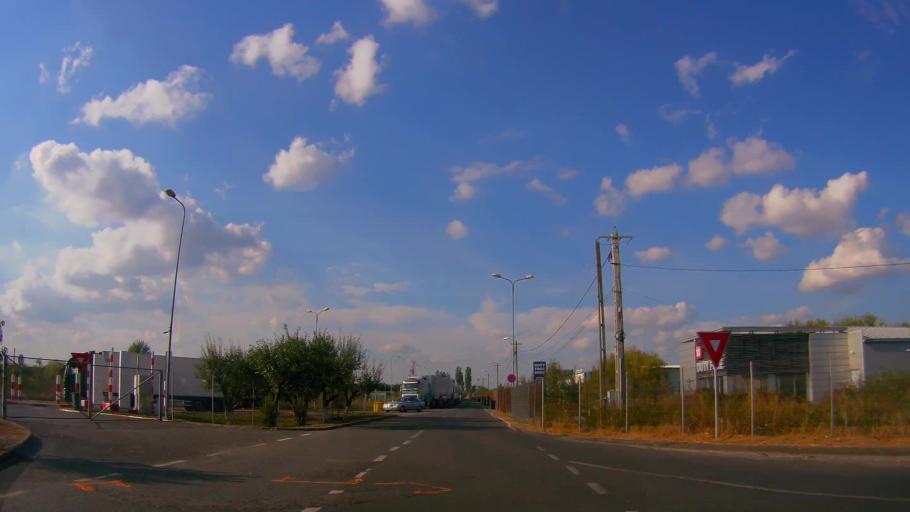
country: RO
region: Satu Mare
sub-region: Comuna Porumbesti
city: Porumbesti
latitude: 47.9940
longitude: 23.0025
